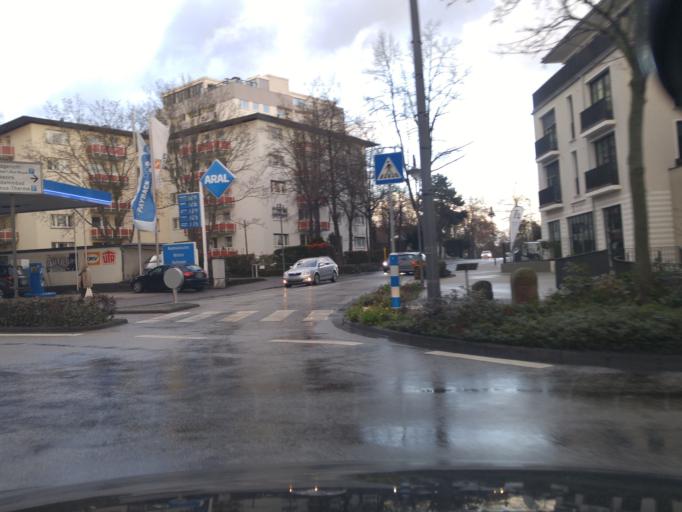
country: DE
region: Hesse
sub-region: Regierungsbezirk Darmstadt
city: Bad Homburg vor der Hoehe
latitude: 50.2212
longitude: 8.6263
